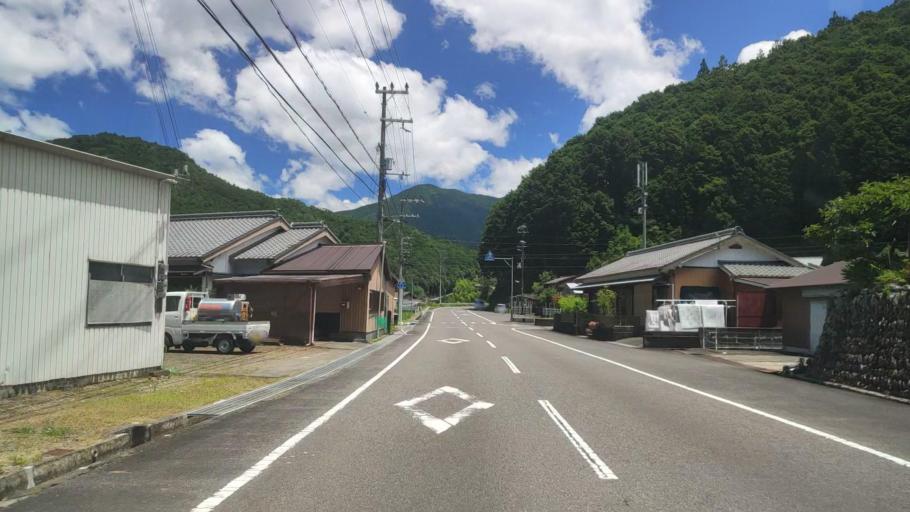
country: JP
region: Mie
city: Owase
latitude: 33.9811
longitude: 136.0343
